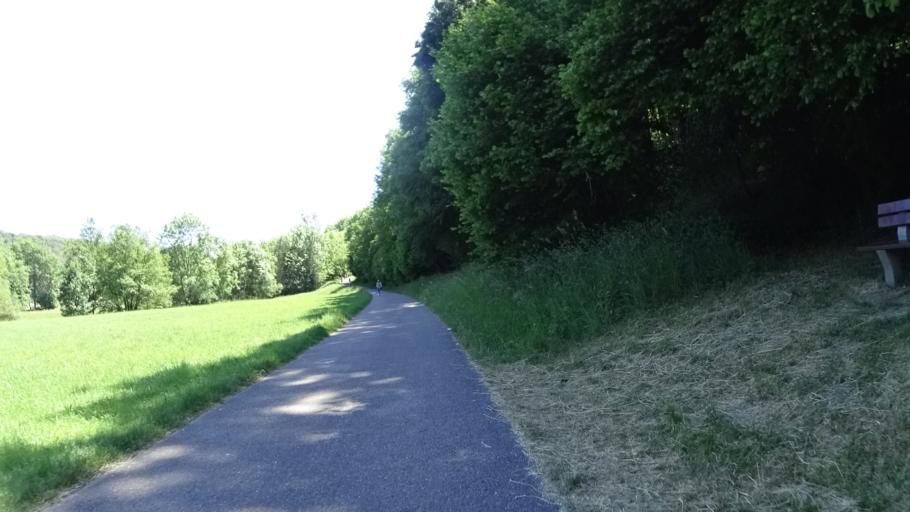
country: DE
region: Bavaria
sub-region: Regierungsbezirk Mittelfranken
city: Adelshofen
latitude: 49.4242
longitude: 10.1448
